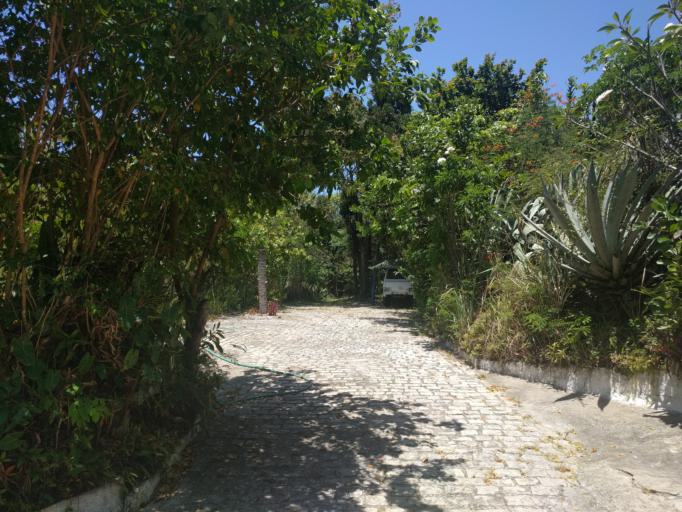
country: BR
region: Rio Grande do Norte
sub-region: Ares
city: Ares
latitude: -6.2268
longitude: -35.0642
